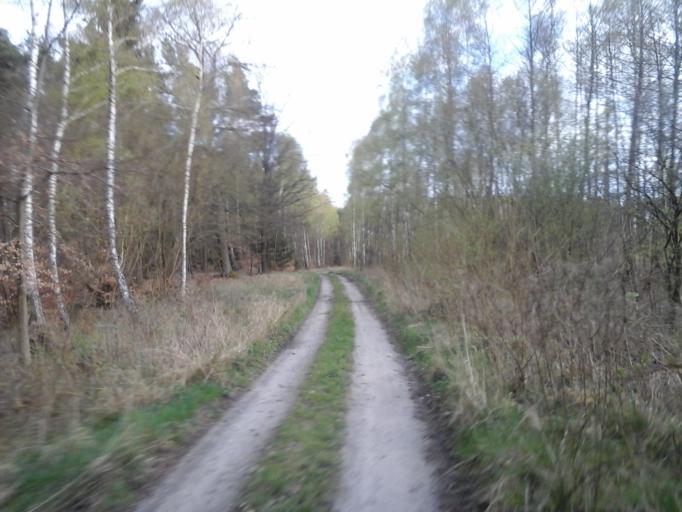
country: PL
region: West Pomeranian Voivodeship
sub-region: Powiat choszczenski
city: Bierzwnik
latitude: 53.0312
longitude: 15.6009
